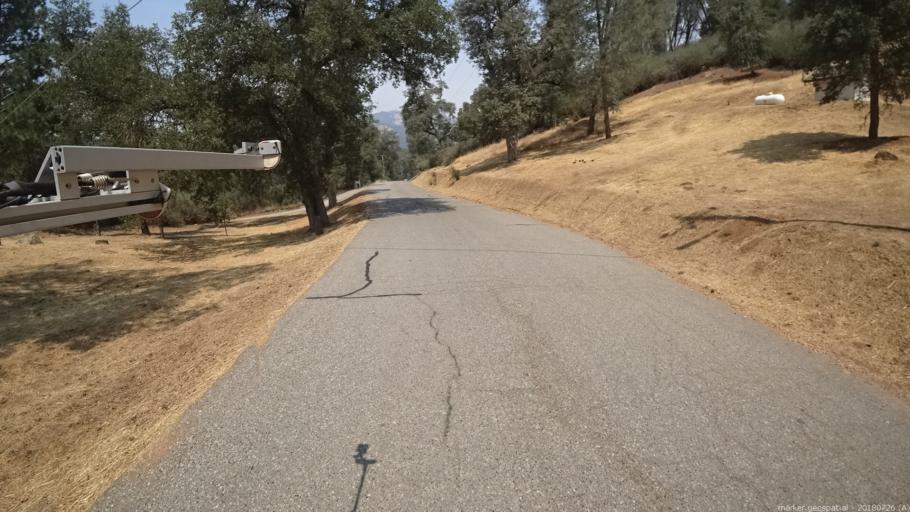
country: US
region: California
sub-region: Madera County
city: Oakhurst
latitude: 37.2839
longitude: -119.6517
